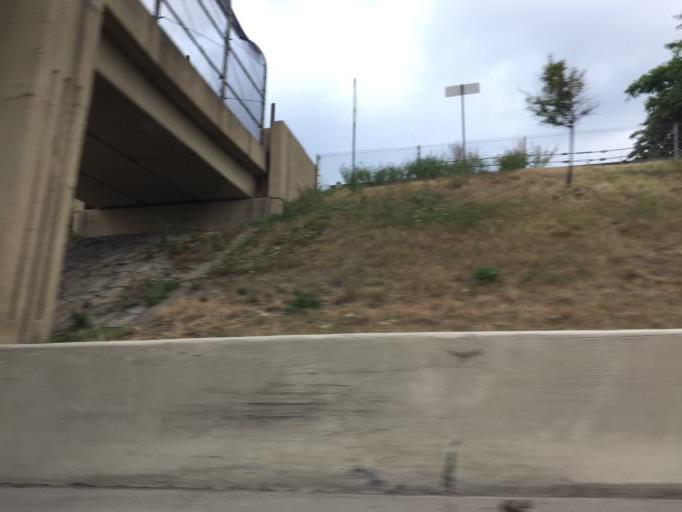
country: US
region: Michigan
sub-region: Wayne County
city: Highland Park
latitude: 42.3756
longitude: -83.0873
